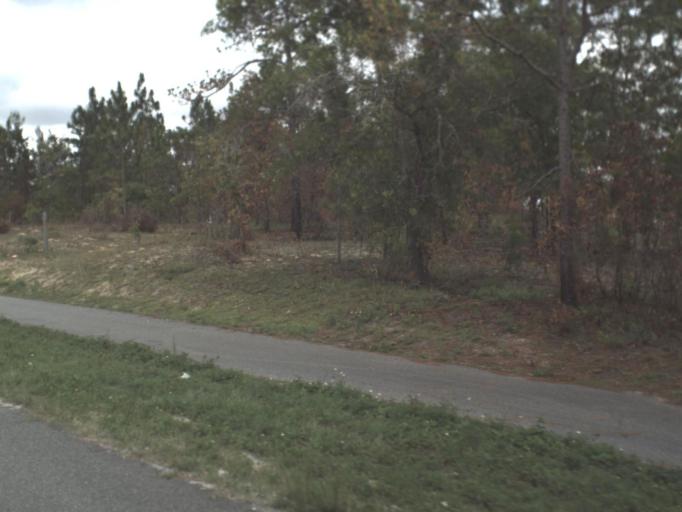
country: US
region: Florida
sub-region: Clay County
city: Keystone Heights
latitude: 29.8354
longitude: -81.9773
